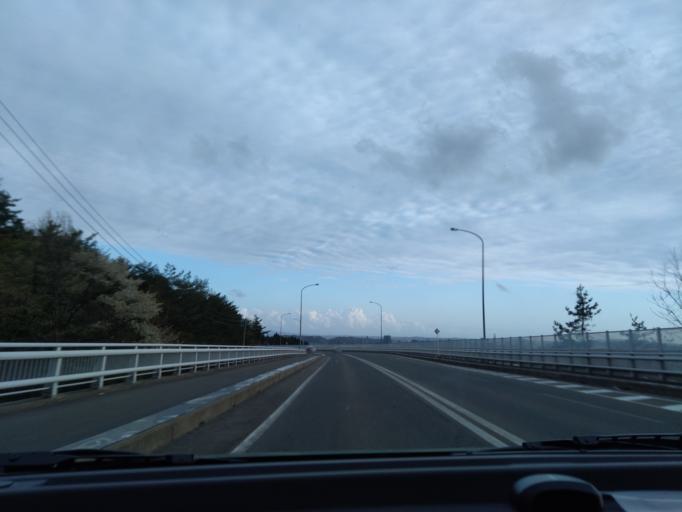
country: JP
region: Akita
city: Akita
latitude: 39.7370
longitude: 140.1365
